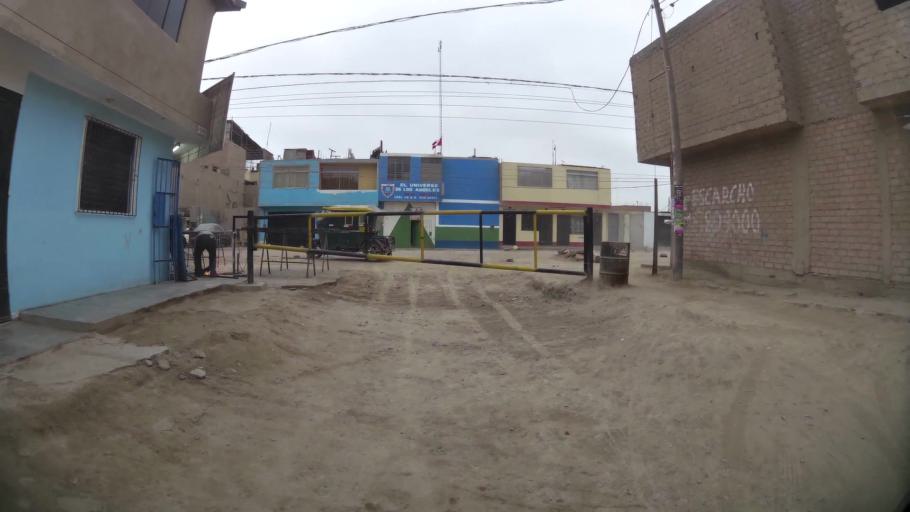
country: PE
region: Lima
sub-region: Lima
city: Independencia
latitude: -11.9733
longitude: -77.0908
